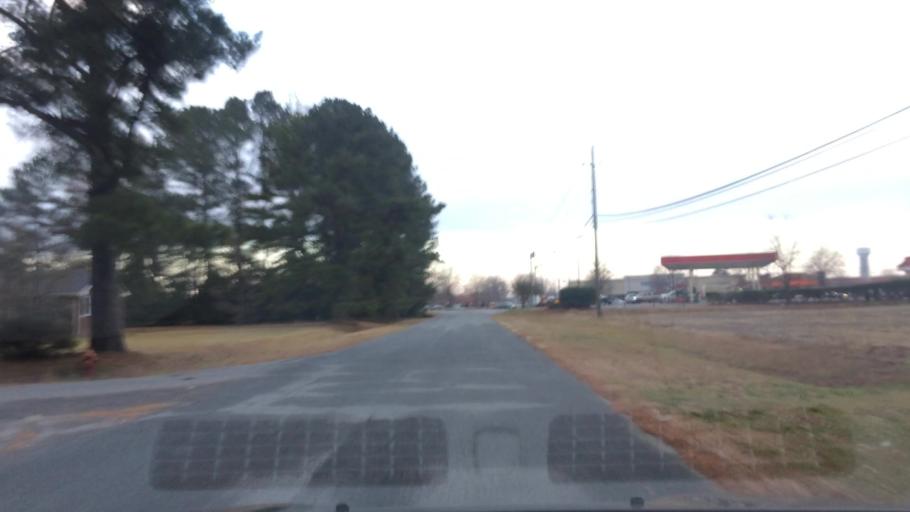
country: US
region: North Carolina
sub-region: Pitt County
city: Ayden
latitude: 35.4742
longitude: -77.4367
